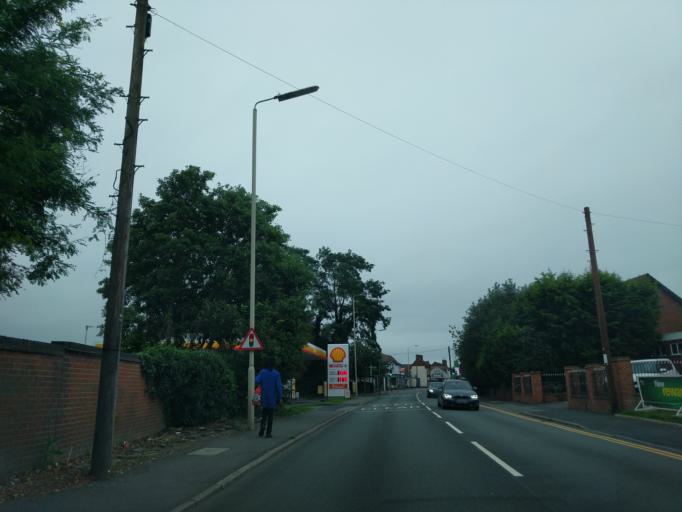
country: GB
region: England
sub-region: Dudley
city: Stourbridge
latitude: 52.4463
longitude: -2.1404
